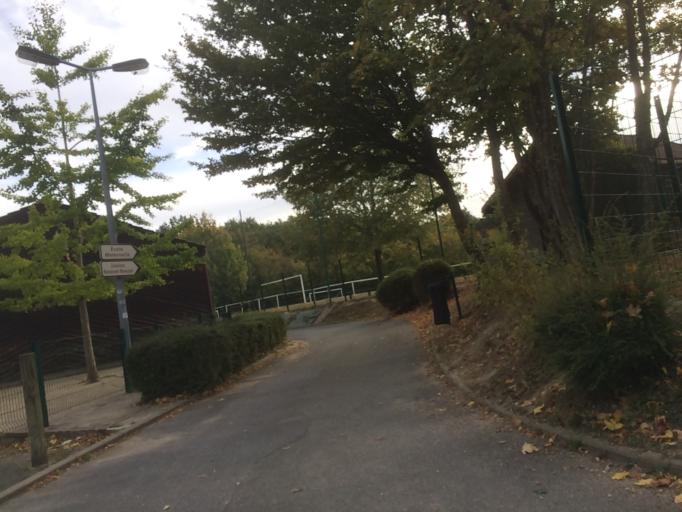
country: FR
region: Ile-de-France
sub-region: Departement de l'Essonne
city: Gometz-le-Chatel
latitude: 48.6751
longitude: 2.1417
